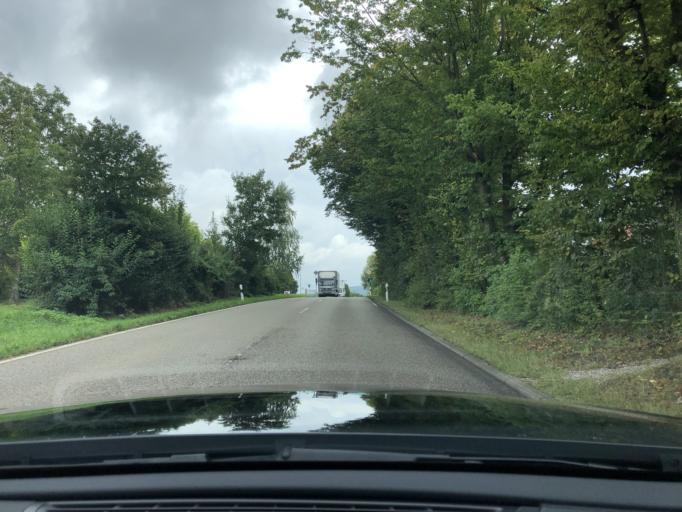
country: DE
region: Baden-Wuerttemberg
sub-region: Regierungsbezirk Stuttgart
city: Marbach am Neckar
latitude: 48.9360
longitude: 9.2702
